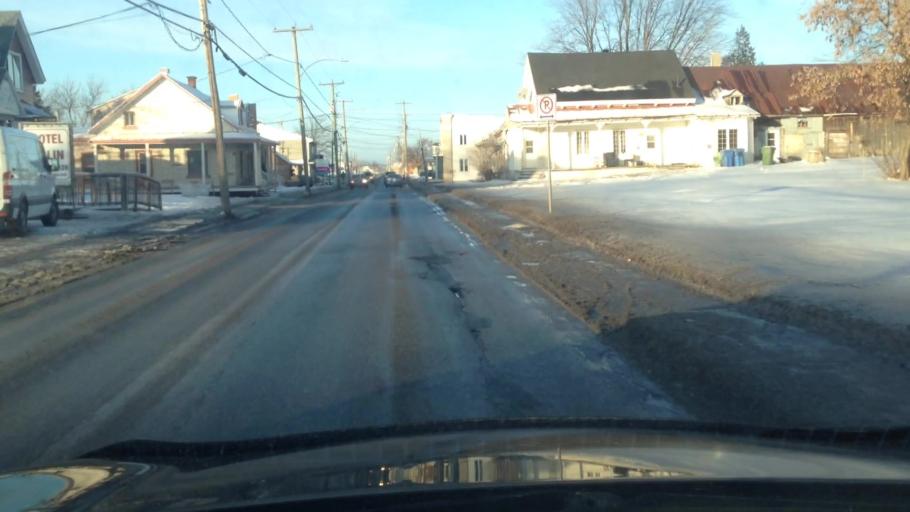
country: CA
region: Quebec
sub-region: Lanaudiere
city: Saint-Lin-Laurentides
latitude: 45.8569
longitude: -73.7571
